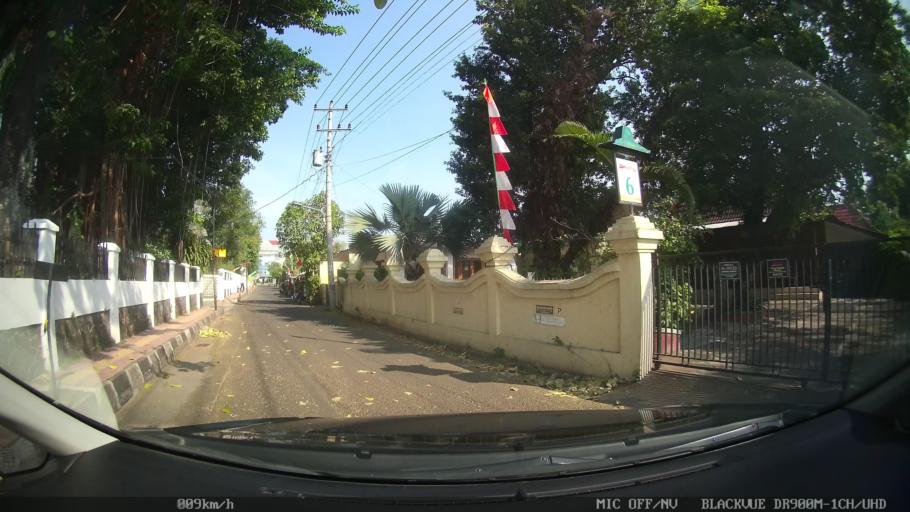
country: ID
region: Daerah Istimewa Yogyakarta
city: Yogyakarta
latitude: -7.7995
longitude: 110.3541
